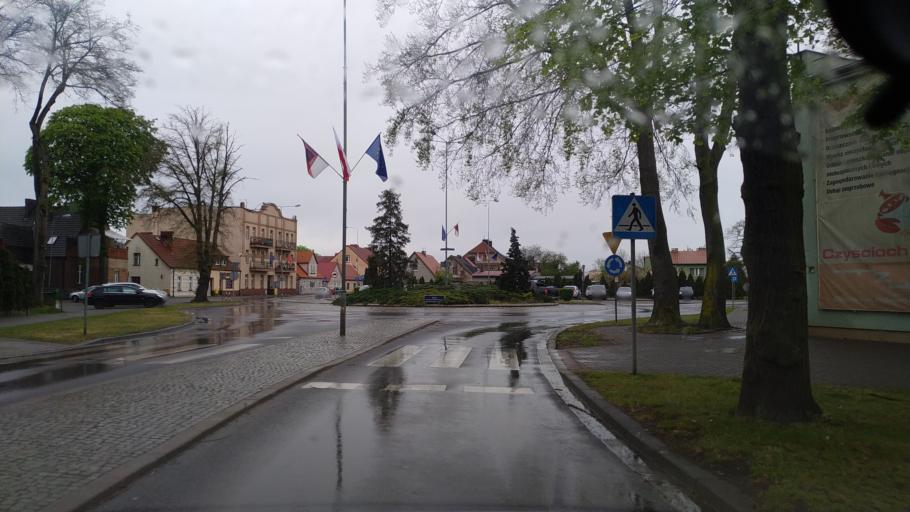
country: PL
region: Greater Poland Voivodeship
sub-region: Powiat zlotowski
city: Zlotow
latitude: 53.3585
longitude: 17.0356
